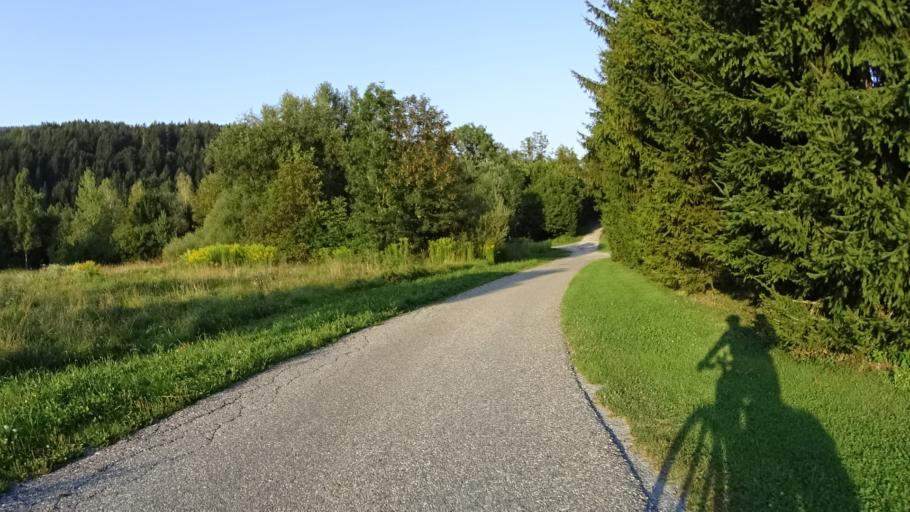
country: AT
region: Carinthia
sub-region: Politischer Bezirk Klagenfurt Land
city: Ludmannsdorf
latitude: 46.5365
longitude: 14.1103
